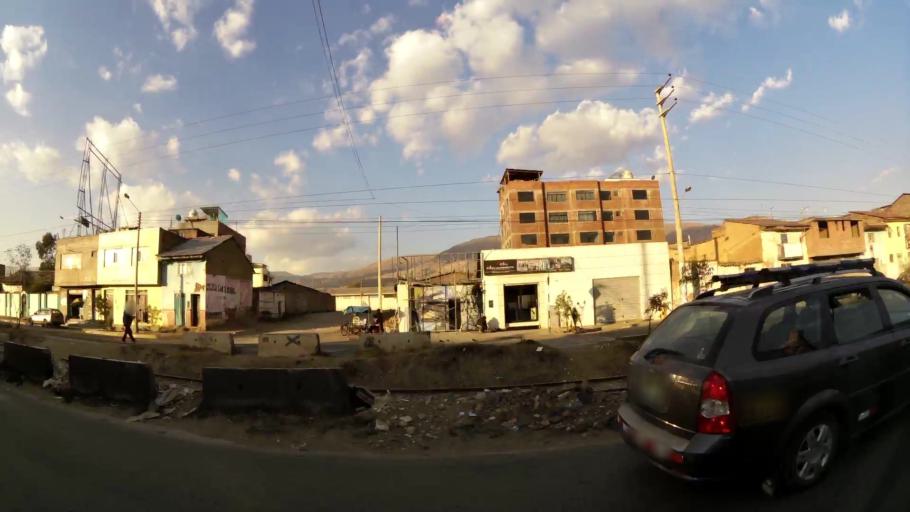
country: PE
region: Junin
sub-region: Provincia de Huancayo
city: Huancayo
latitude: -12.0573
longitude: -75.2116
